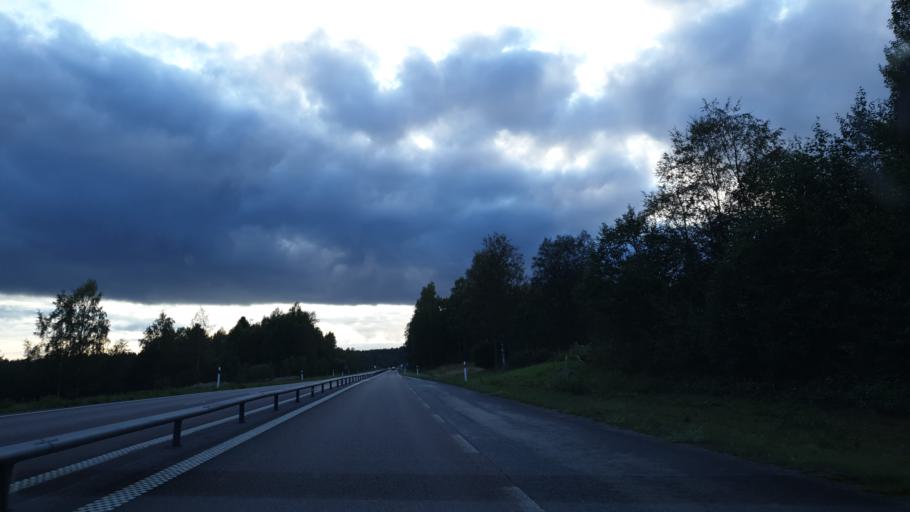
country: SE
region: Vaesternorrland
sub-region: OErnskoeldsviks Kommun
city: Husum
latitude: 63.3472
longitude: 19.1387
